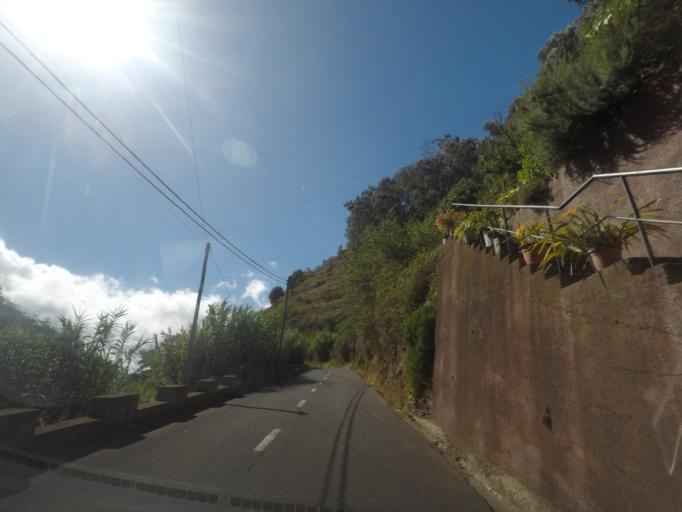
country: PT
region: Madeira
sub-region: Ribeira Brava
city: Campanario
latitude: 32.6888
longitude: -17.0282
